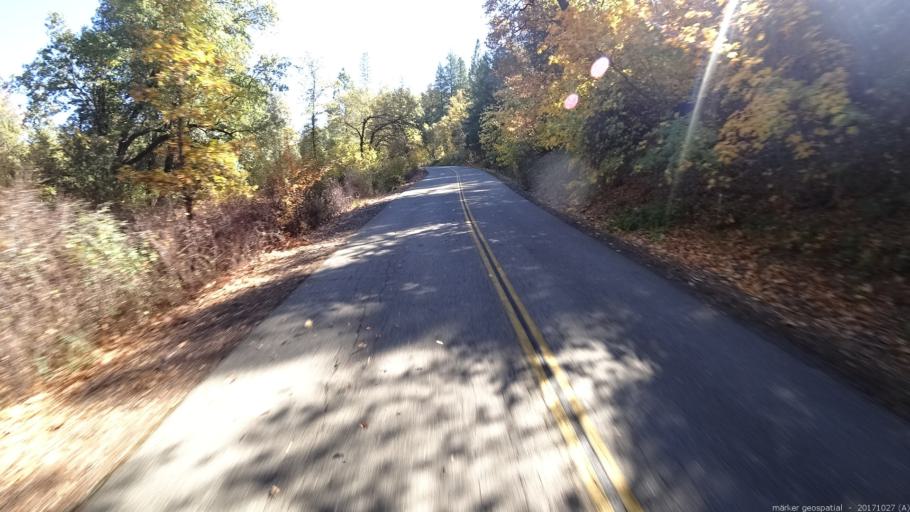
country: US
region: California
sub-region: Shasta County
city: Bella Vista
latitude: 40.7384
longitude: -122.0104
